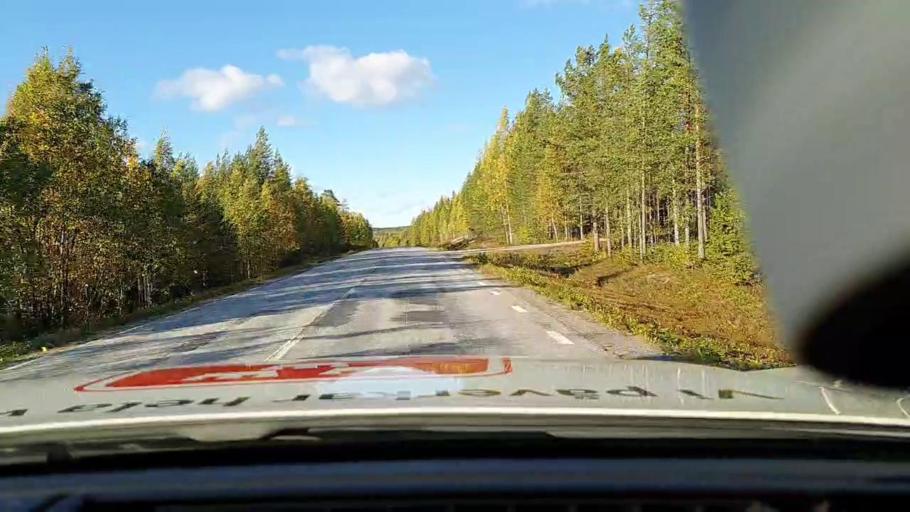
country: SE
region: Norrbotten
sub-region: Pitea Kommun
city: Norrfjarden
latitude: 65.4545
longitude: 21.4559
